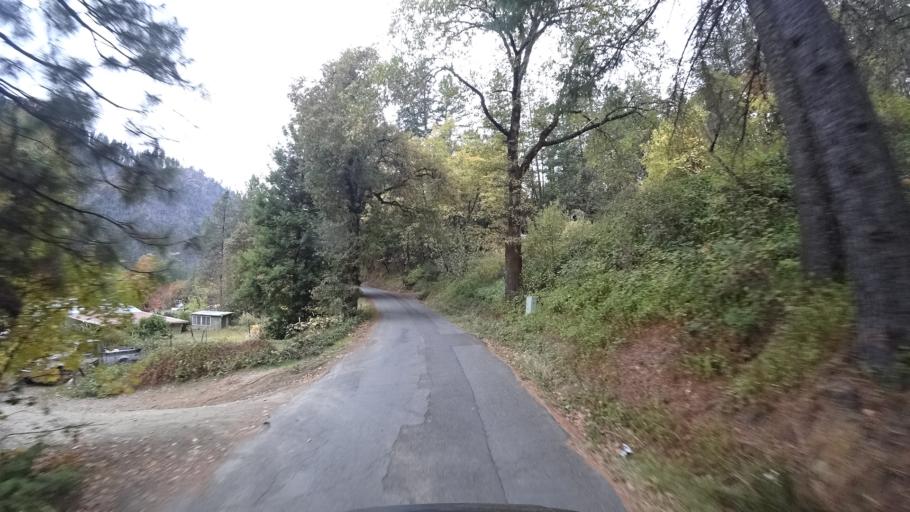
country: US
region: California
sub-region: Siskiyou County
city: Happy Camp
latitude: 41.7918
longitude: -123.3831
